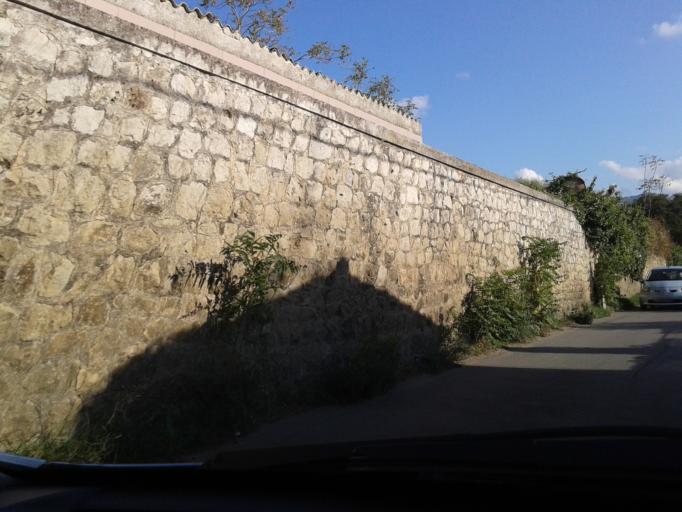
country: IT
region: Sicily
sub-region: Palermo
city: Monreale
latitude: 38.1020
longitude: 13.3159
